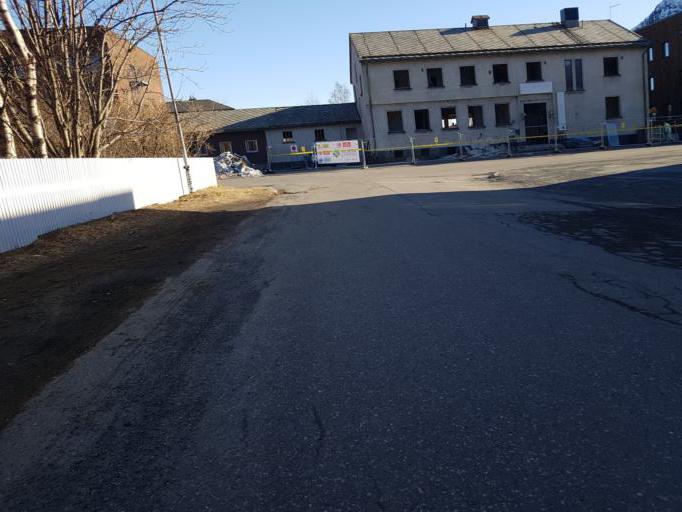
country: NO
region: Nordland
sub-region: Vefsn
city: Mosjoen
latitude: 65.8386
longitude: 13.1997
